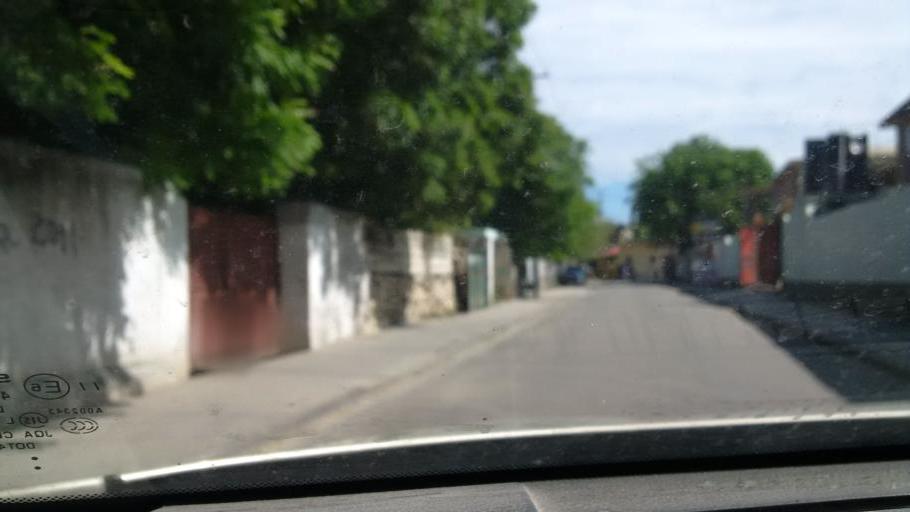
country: HT
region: Ouest
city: Port-au-Prince
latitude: 18.5352
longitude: -72.3323
